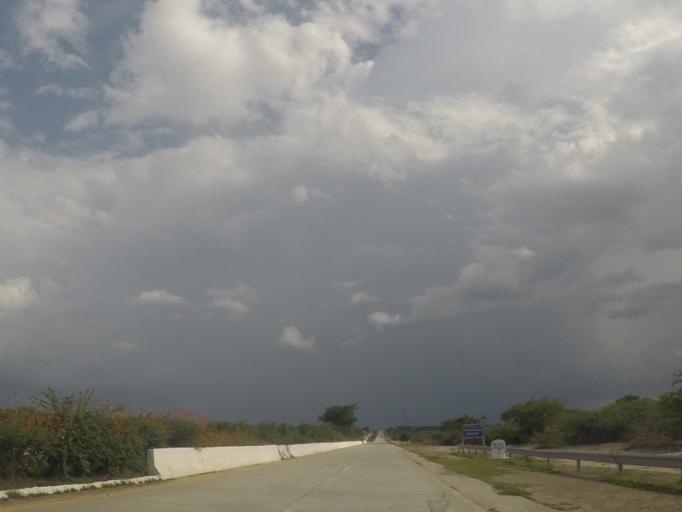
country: MM
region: Mandalay
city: Meiktila
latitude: 21.1084
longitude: 95.7964
